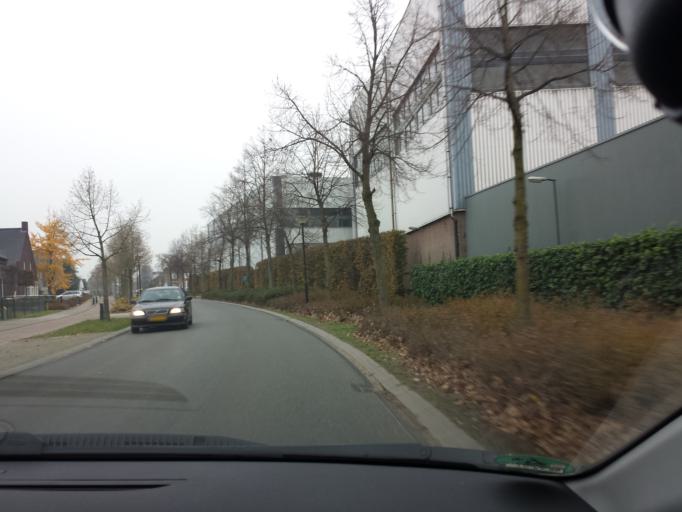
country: NL
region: Limburg
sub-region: Gemeente Venray
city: Venray
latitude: 51.5687
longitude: 6.0363
